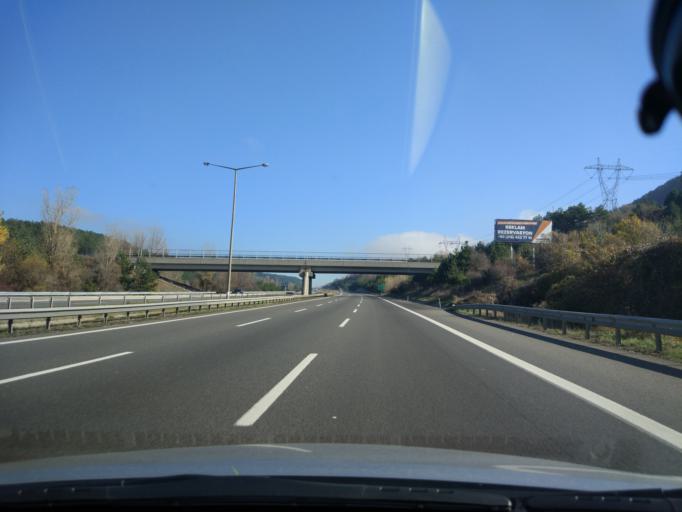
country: TR
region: Bolu
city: Yenicaga
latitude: 40.7437
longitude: 31.8671
